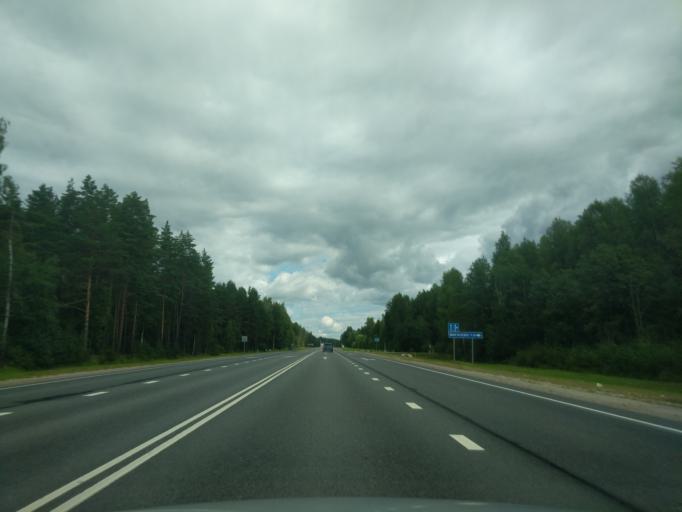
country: RU
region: Jaroslavl
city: Nekrasovskoye
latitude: 57.5919
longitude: 40.3020
